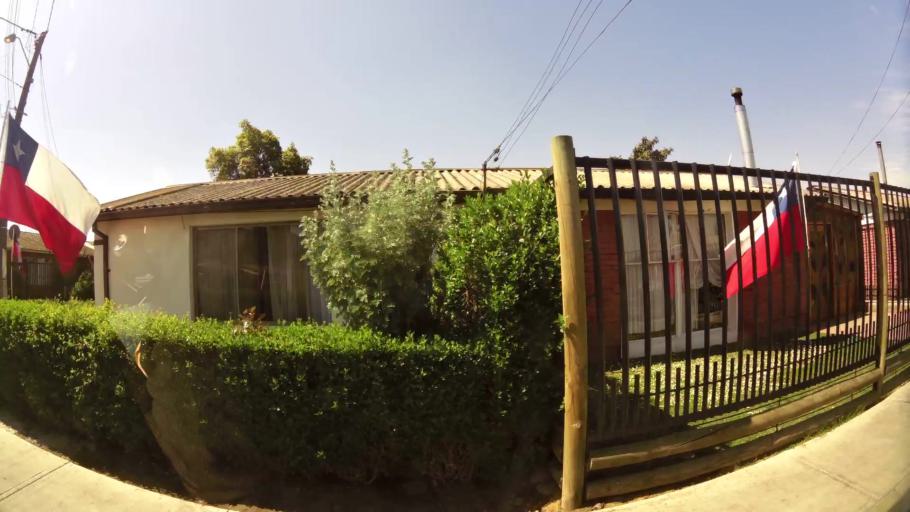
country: CL
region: Santiago Metropolitan
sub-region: Provincia de Talagante
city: Talagante
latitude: -33.6493
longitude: -70.9273
